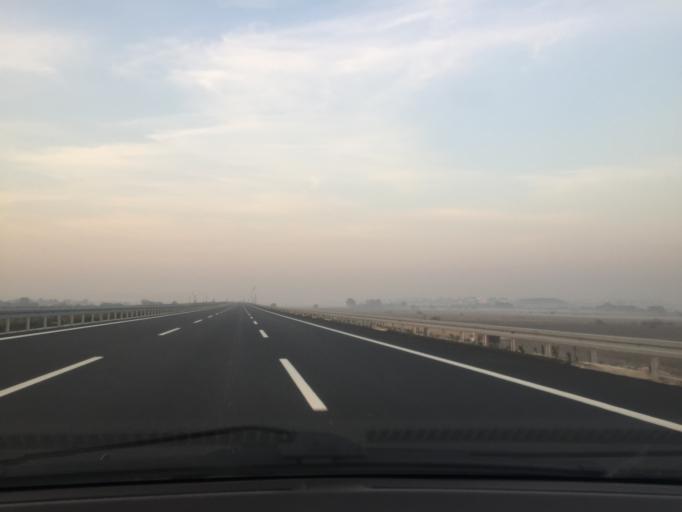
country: TR
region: Bursa
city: Karacabey
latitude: 40.2284
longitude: 28.4108
